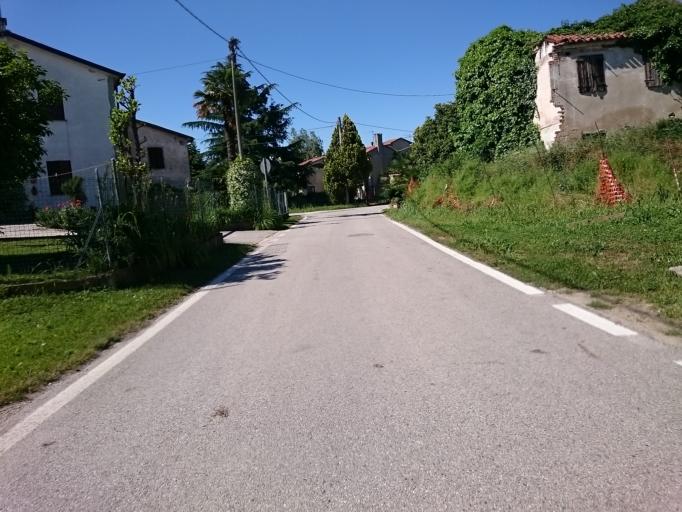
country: IT
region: Veneto
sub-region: Provincia di Padova
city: Saonara
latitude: 45.3555
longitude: 12.0034
